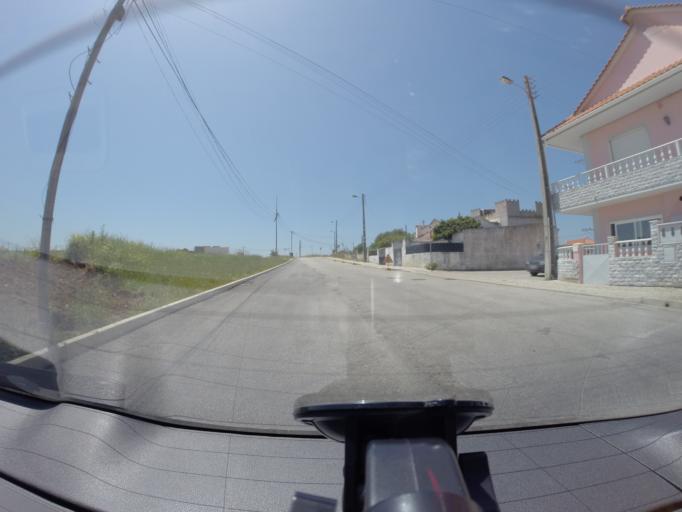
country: PT
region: Lisbon
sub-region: Cascais
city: Parede
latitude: 38.7175
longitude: -9.3579
